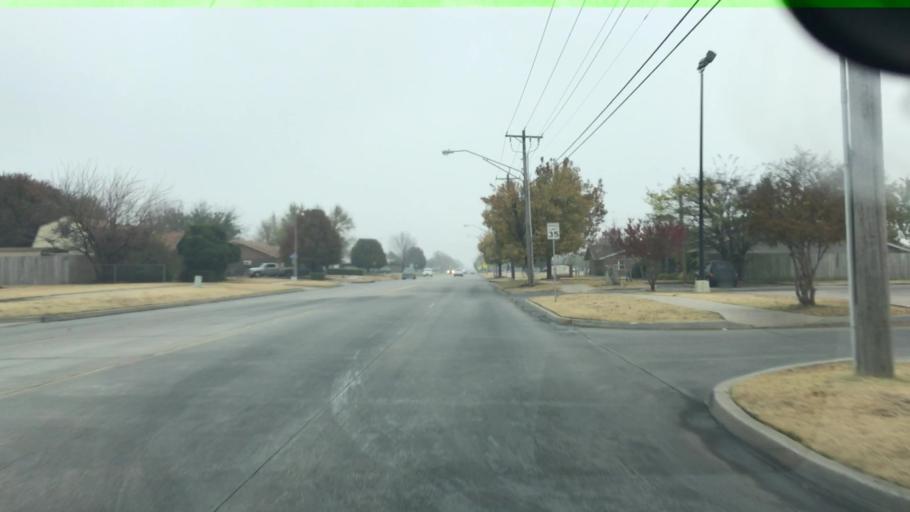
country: US
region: Oklahoma
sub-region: Cleveland County
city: Moore
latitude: 35.3478
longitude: -97.5122
